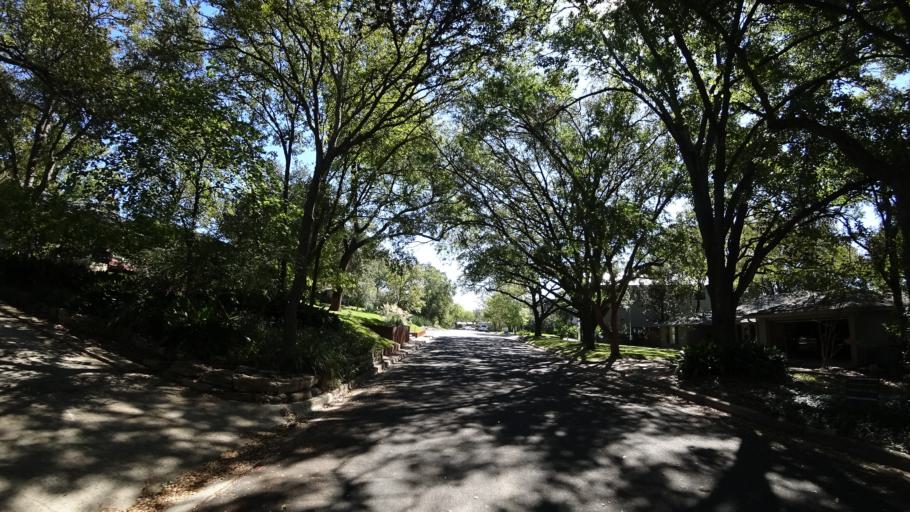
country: US
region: Texas
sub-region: Travis County
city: West Lake Hills
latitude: 30.3167
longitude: -97.7700
